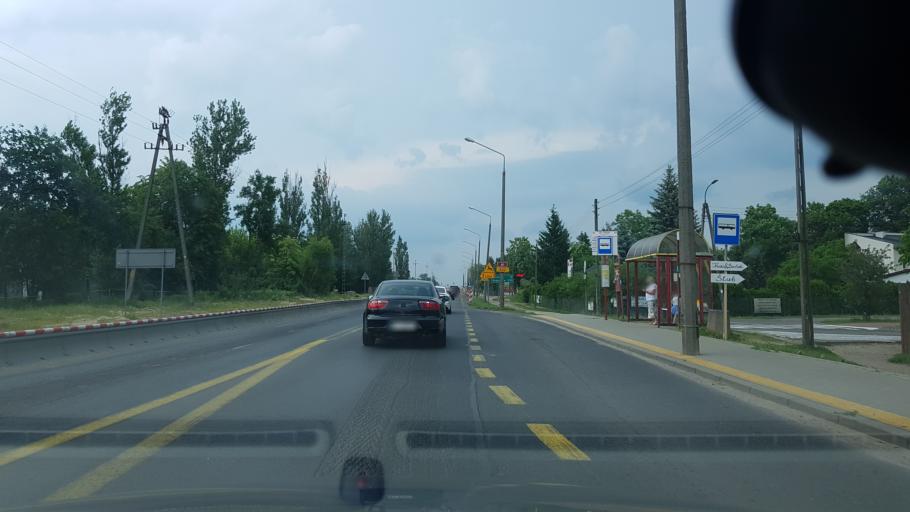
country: PL
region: Masovian Voivodeship
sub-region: Powiat legionowski
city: Michalow-Reginow
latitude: 52.4049
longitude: 20.9508
